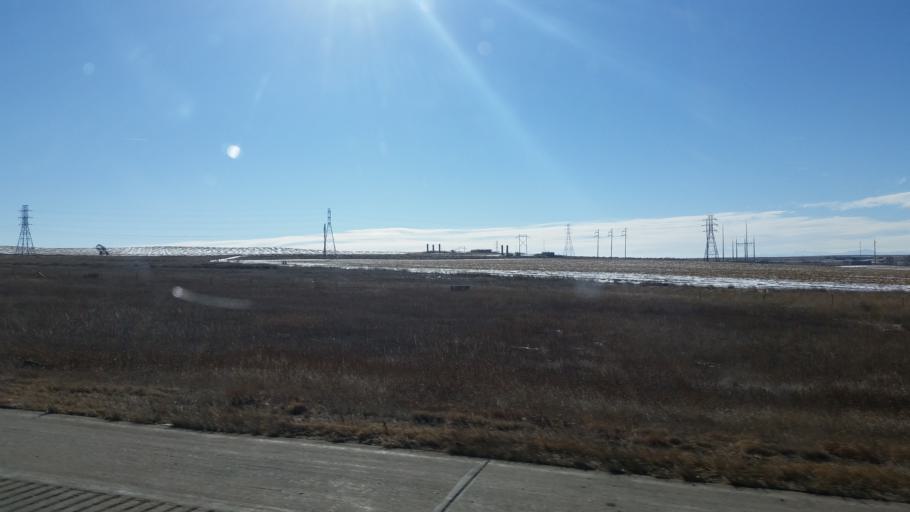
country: US
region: Colorado
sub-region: Weld County
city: Milliken
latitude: 40.4041
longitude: -104.8205
